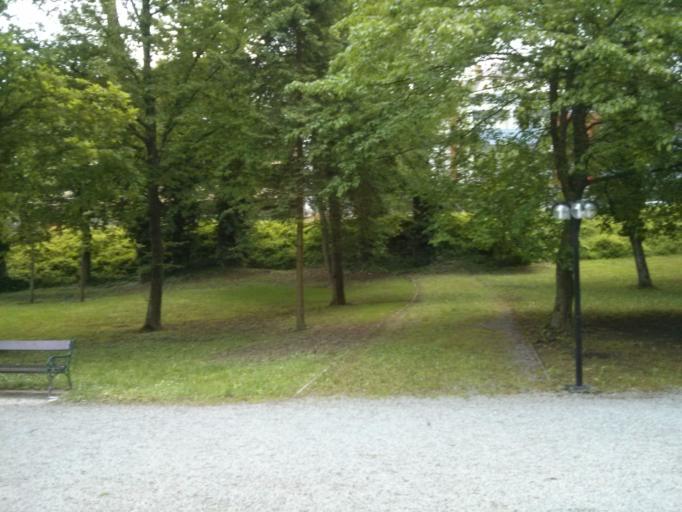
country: AT
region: Burgenland
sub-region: Politischer Bezirk Oberwart
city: Bad Tatzmannsdorf
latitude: 47.3347
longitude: 16.2298
